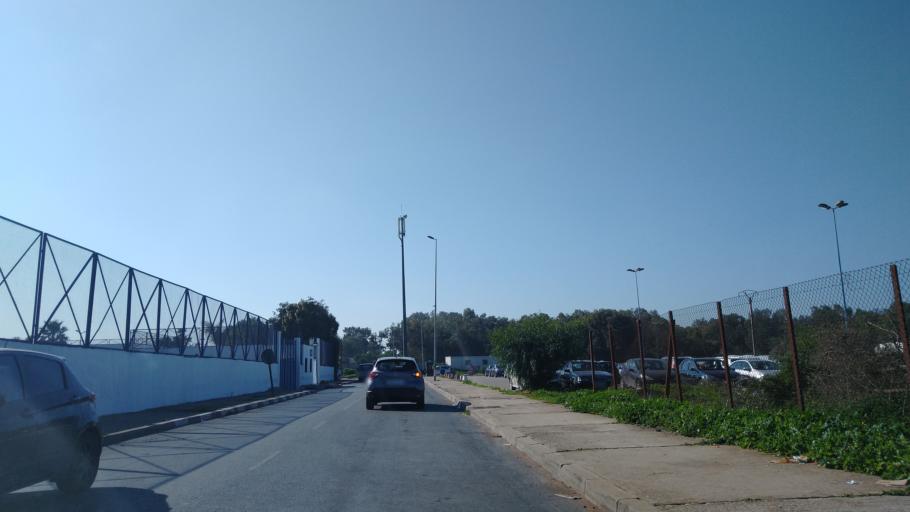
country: MA
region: Rabat-Sale-Zemmour-Zaer
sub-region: Skhirate-Temara
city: Temara
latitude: 33.9542
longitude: -6.8545
